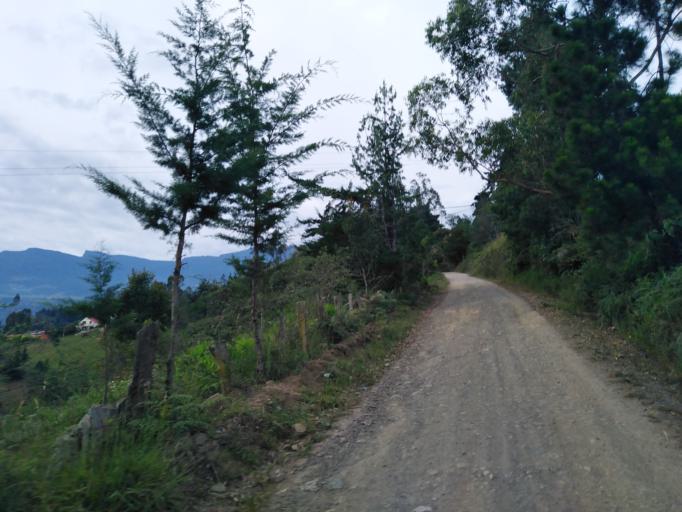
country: CO
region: Cundinamarca
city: Tenza
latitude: 5.0995
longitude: -73.4164
